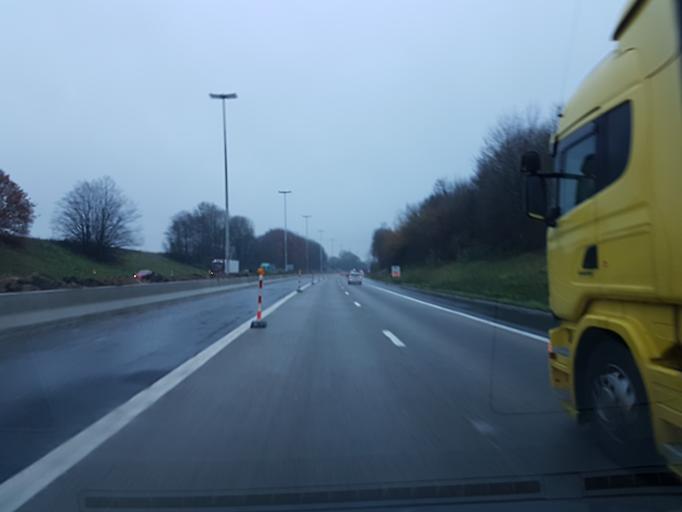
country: BE
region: Wallonia
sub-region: Province de Namur
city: Eghezee
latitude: 50.5246
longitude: 4.9224
